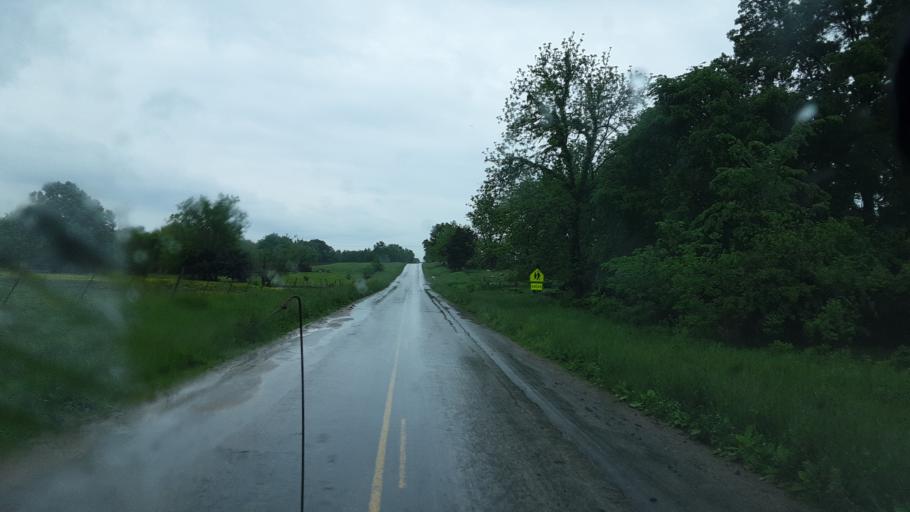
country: US
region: Missouri
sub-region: Randolph County
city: Moberly
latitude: 39.3633
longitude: -92.2681
